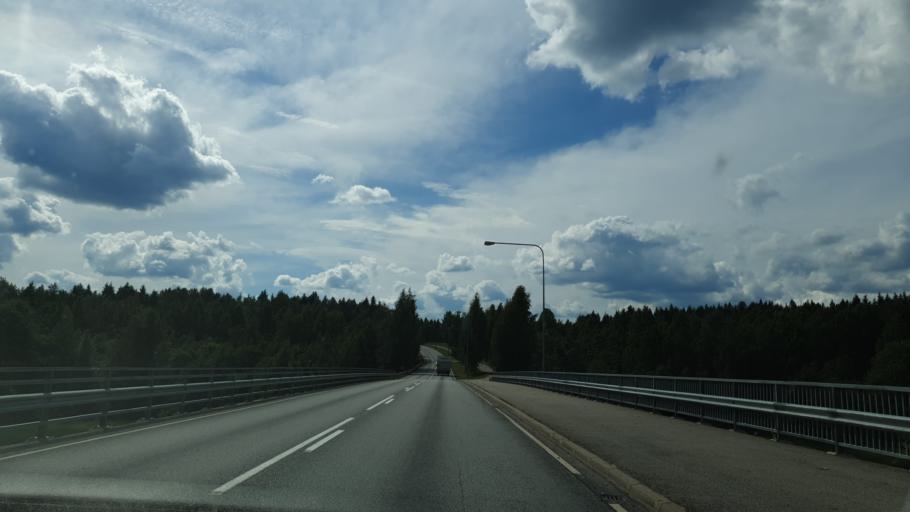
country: FI
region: Kainuu
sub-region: Kajaani
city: Sotkamo
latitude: 64.1696
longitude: 28.4514
